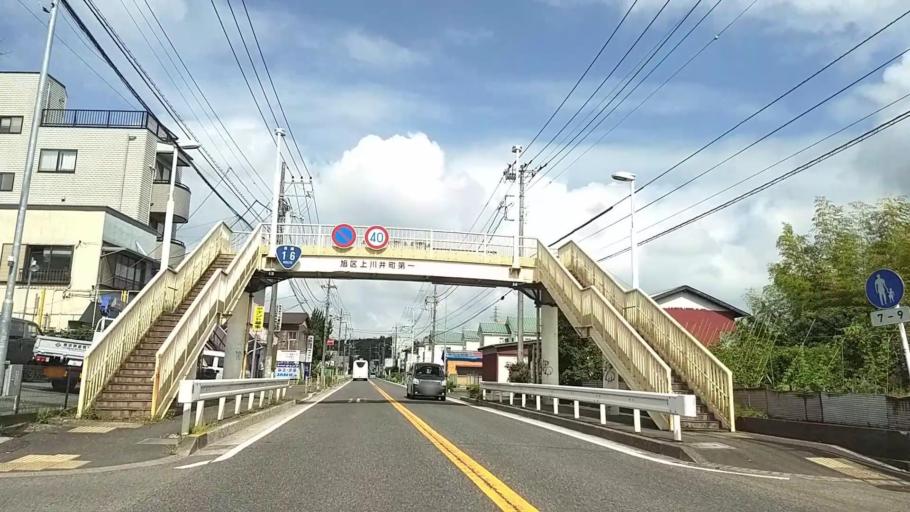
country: JP
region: Kanagawa
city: Minami-rinkan
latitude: 35.4953
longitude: 139.5044
